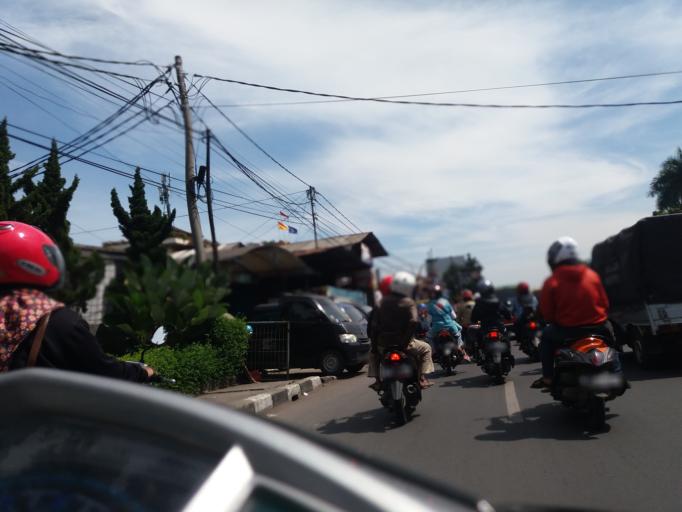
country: ID
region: West Java
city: Margahayukencana
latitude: -6.9482
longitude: 107.6062
